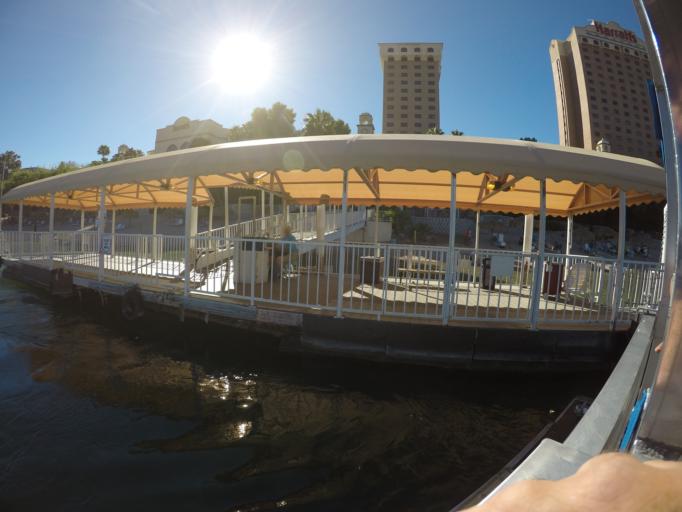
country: US
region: Arizona
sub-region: Mohave County
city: Bullhead City
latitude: 35.1446
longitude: -114.5753
